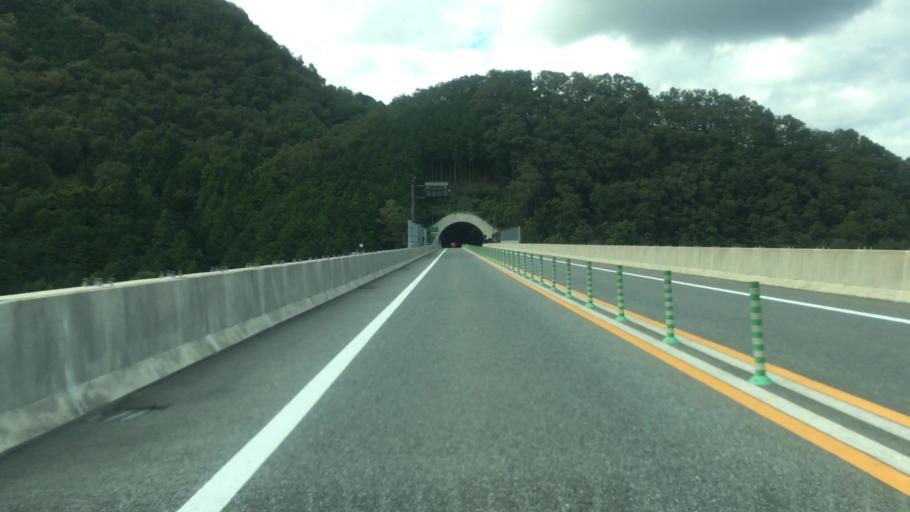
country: JP
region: Hyogo
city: Toyooka
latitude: 35.3201
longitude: 134.8430
